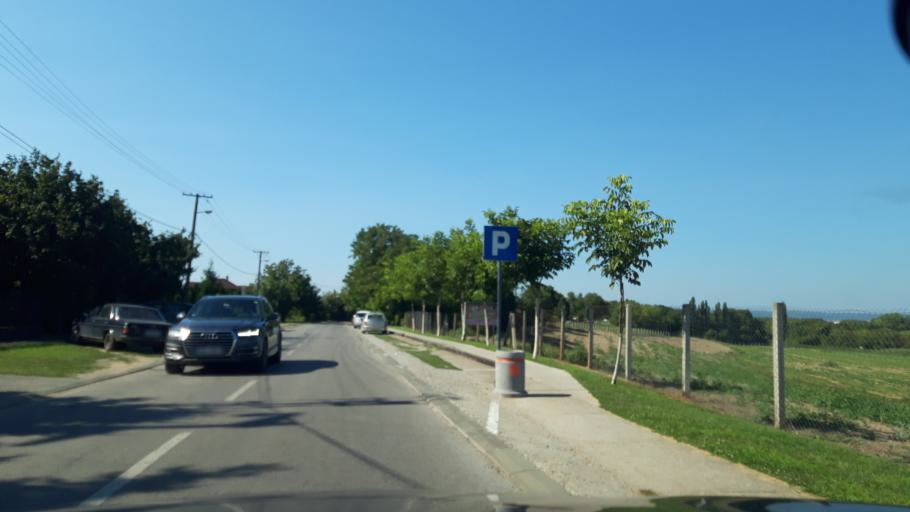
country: RS
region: Autonomna Pokrajina Vojvodina
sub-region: Sremski Okrug
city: Ruma
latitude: 45.0231
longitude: 19.8215
